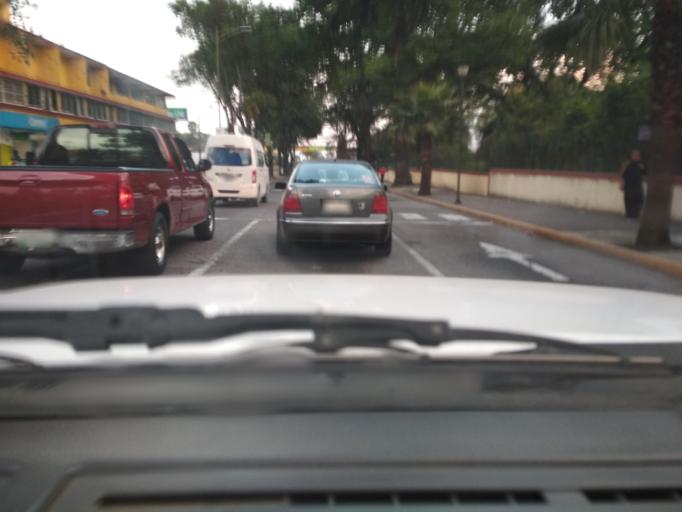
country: MX
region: Veracruz
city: Orizaba
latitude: 18.8613
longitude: -97.0960
